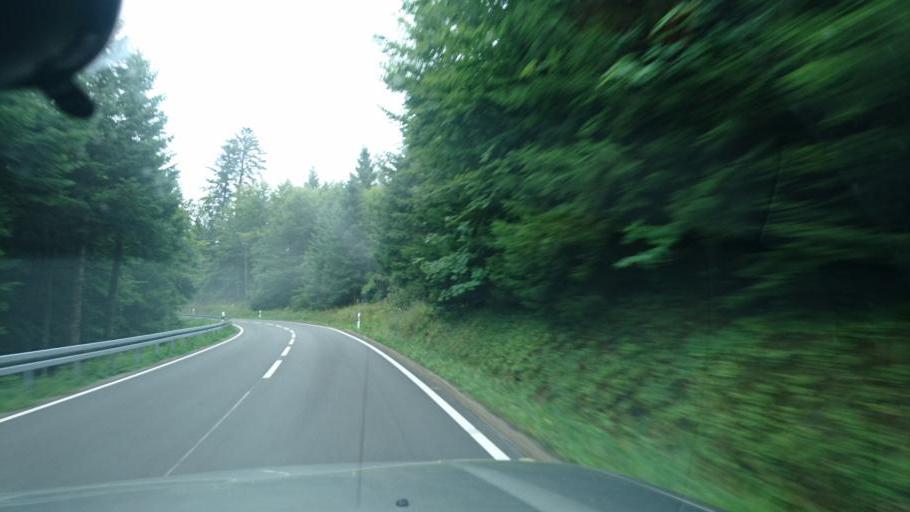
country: DE
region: Baden-Wuerttemberg
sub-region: Karlsruhe Region
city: Baiersbronn
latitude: 48.5227
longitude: 8.4243
